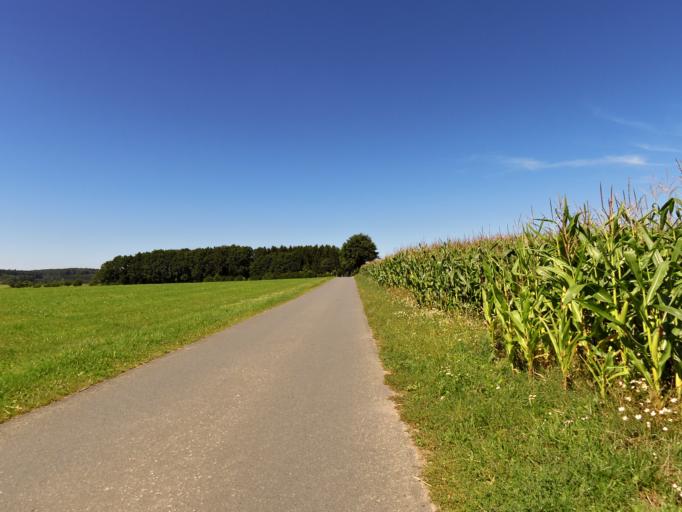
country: DE
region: Hesse
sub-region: Regierungsbezirk Darmstadt
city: Erbach
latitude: 49.6774
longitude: 8.9394
